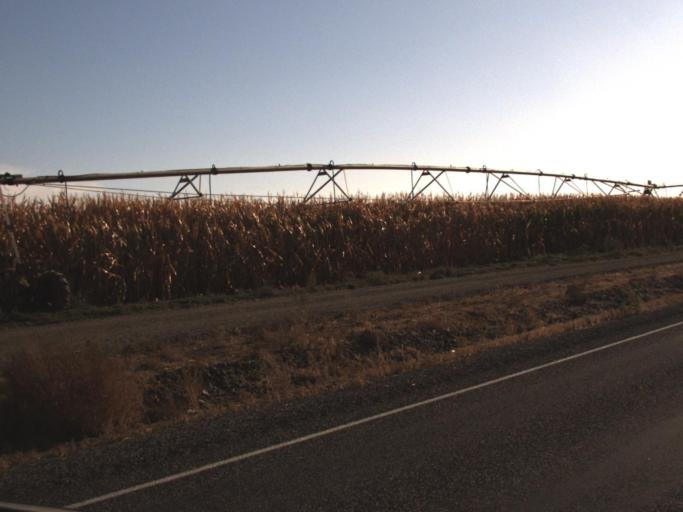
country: US
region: Washington
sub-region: Walla Walla County
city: Burbank
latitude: 46.2503
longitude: -118.8103
